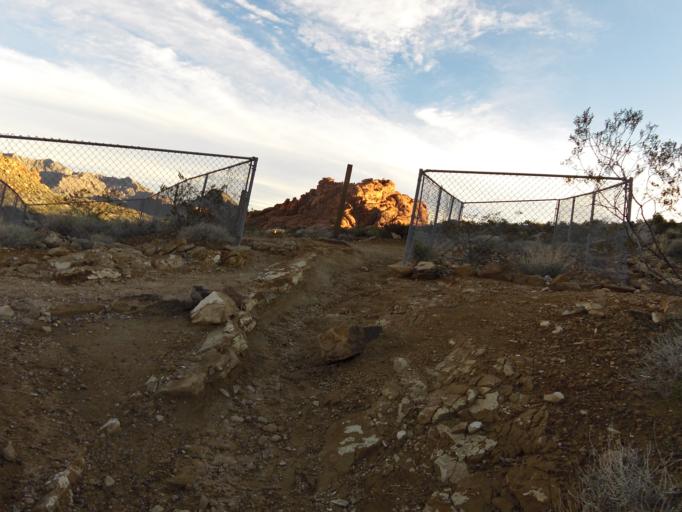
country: US
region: Nevada
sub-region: Clark County
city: Moapa Valley
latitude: 36.4228
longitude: -114.5404
